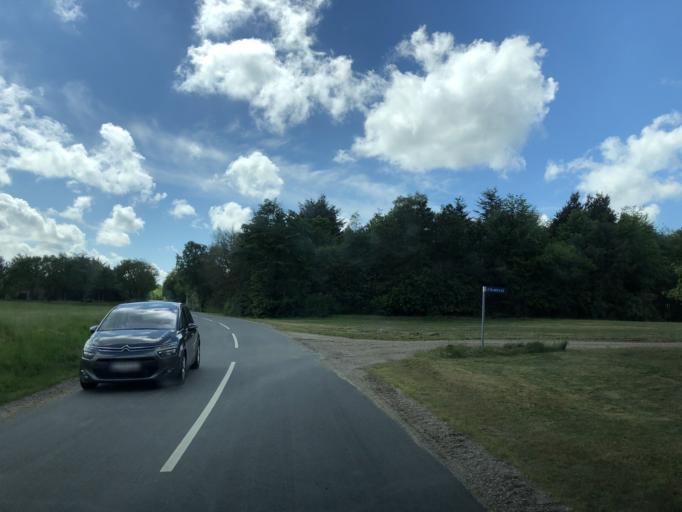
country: DK
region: Central Jutland
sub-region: Ringkobing-Skjern Kommune
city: Tarm
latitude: 55.9429
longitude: 8.5728
